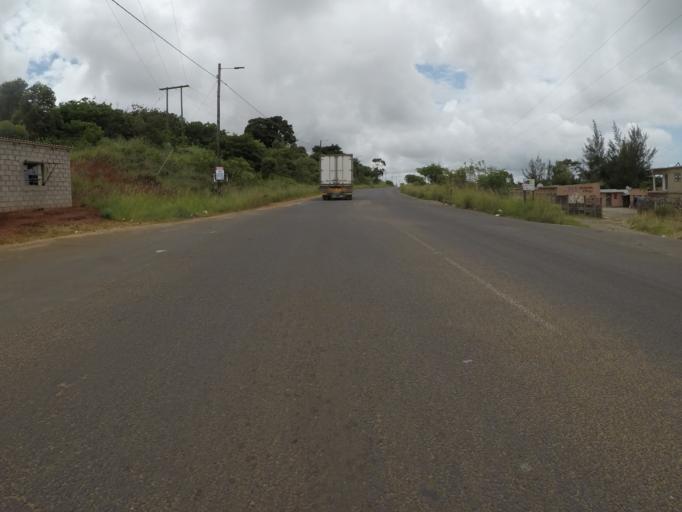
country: ZA
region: KwaZulu-Natal
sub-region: uThungulu District Municipality
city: eSikhawini
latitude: -28.8530
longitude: 31.9236
